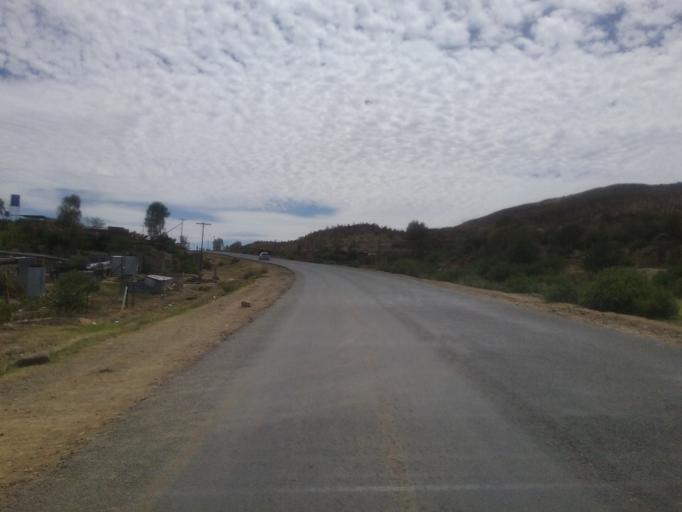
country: LS
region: Mafeteng
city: Mafeteng
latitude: -29.8397
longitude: 27.2323
